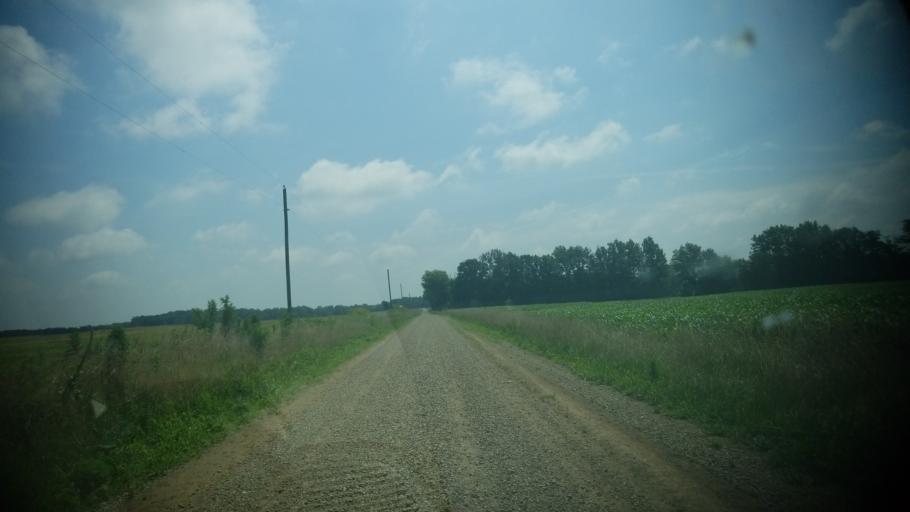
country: US
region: Illinois
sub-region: Wayne County
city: Fairfield
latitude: 38.5298
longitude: -88.3774
